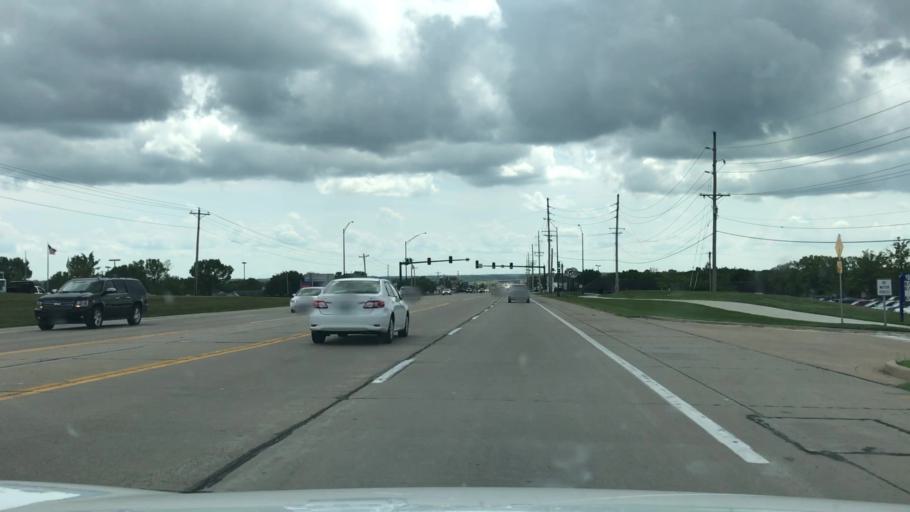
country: US
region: Missouri
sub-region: Saint Charles County
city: Dardenne Prairie
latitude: 38.7728
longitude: -90.7002
